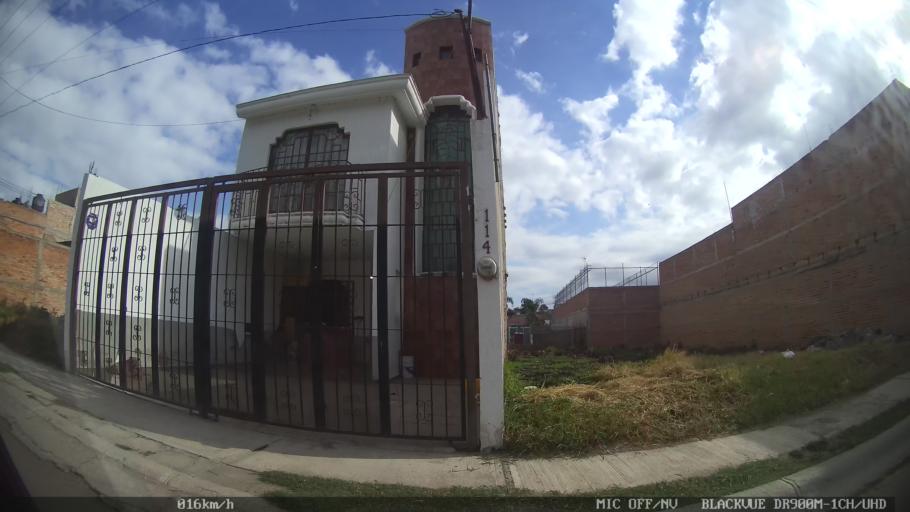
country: MX
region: Jalisco
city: Tonala
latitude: 20.6595
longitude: -103.2339
